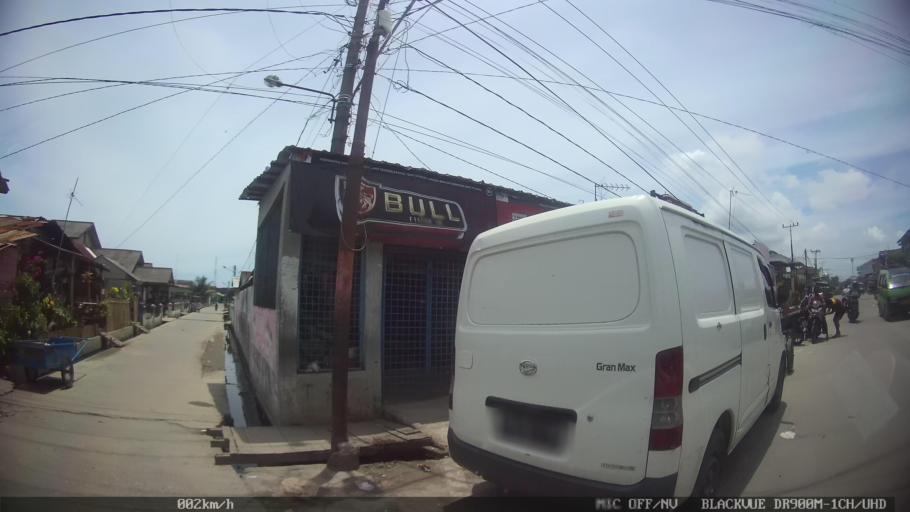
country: ID
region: North Sumatra
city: Belawan
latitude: 3.7764
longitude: 98.7024
